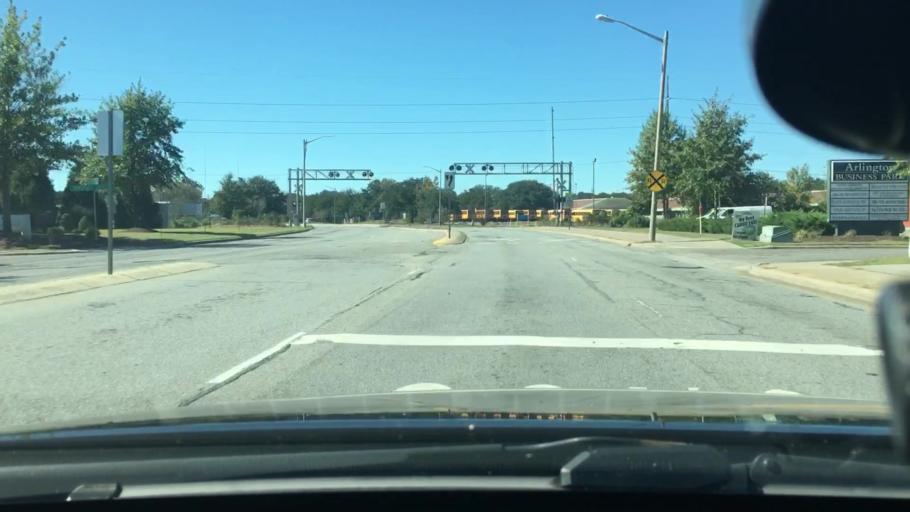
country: US
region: North Carolina
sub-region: Pitt County
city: Greenville
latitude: 35.5918
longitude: -77.3815
